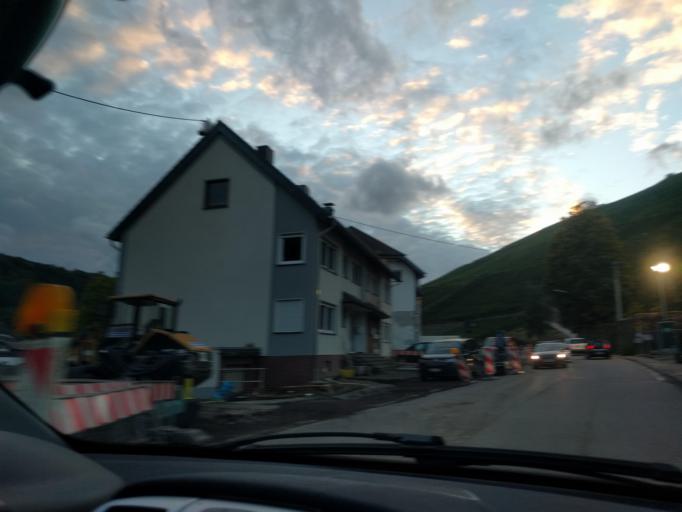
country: DE
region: Rheinland-Pfalz
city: Dernau
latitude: 50.5354
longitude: 7.0574
